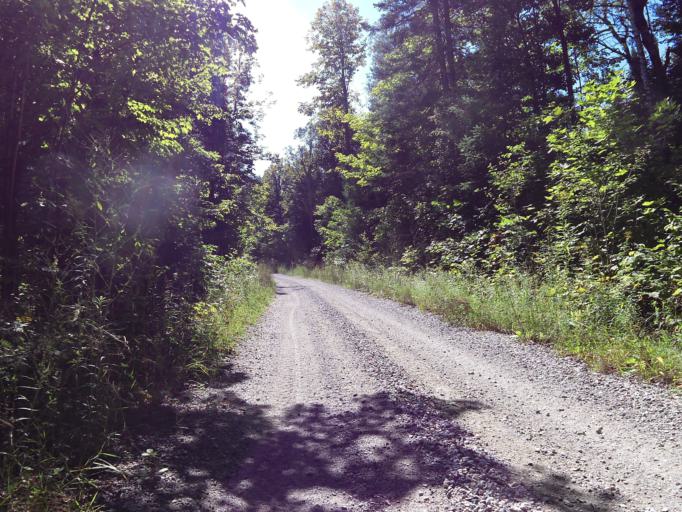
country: CA
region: Ontario
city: Renfrew
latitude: 45.0343
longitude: -76.7058
